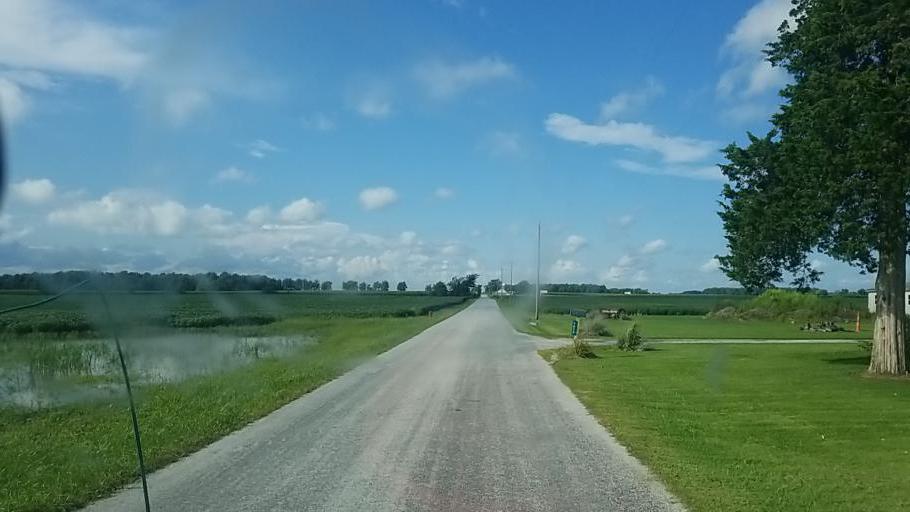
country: US
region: Ohio
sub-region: Hardin County
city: Kenton
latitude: 40.6754
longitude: -83.5310
